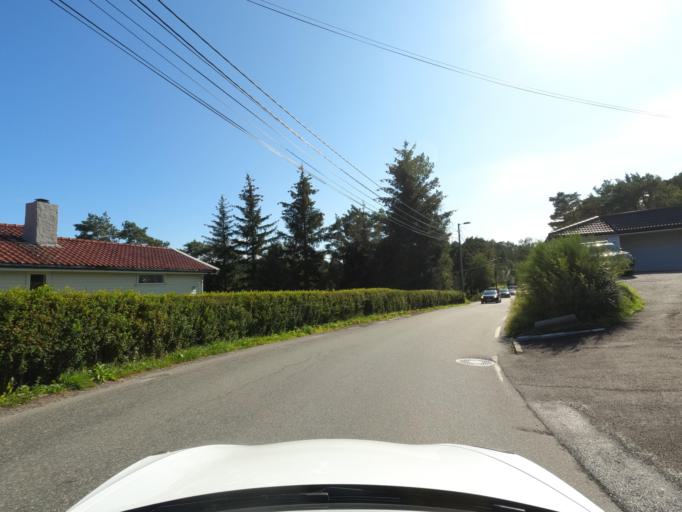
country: NO
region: Hordaland
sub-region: Bergen
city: Sandsli
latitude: 60.2623
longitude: 5.2633
